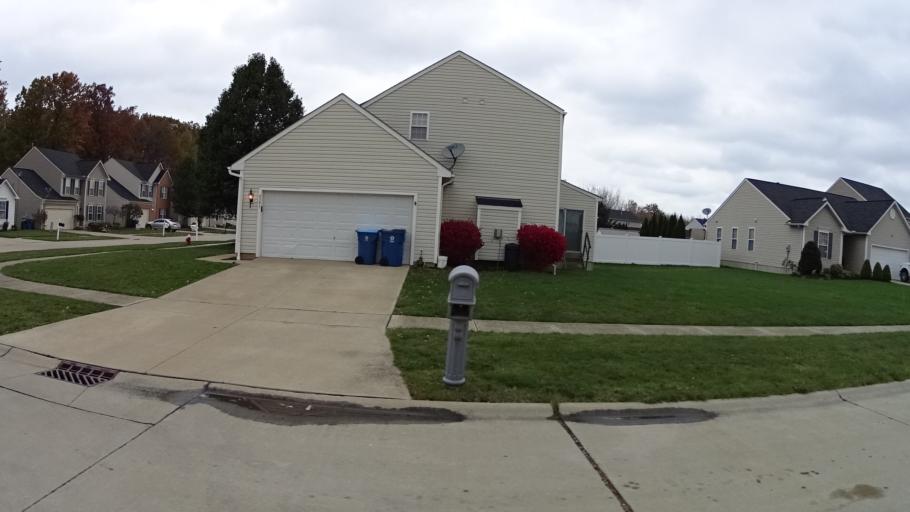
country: US
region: Ohio
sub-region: Lorain County
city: Amherst
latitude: 41.4309
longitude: -82.2275
